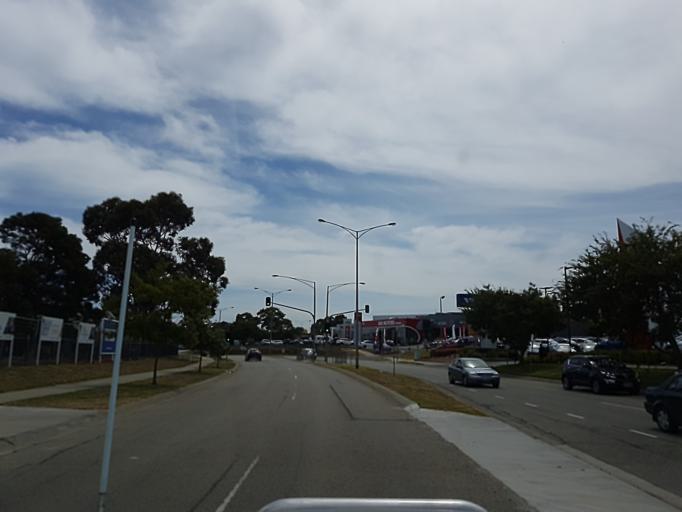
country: AU
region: Victoria
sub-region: Casey
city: Berwick
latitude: -38.0413
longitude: 145.3442
